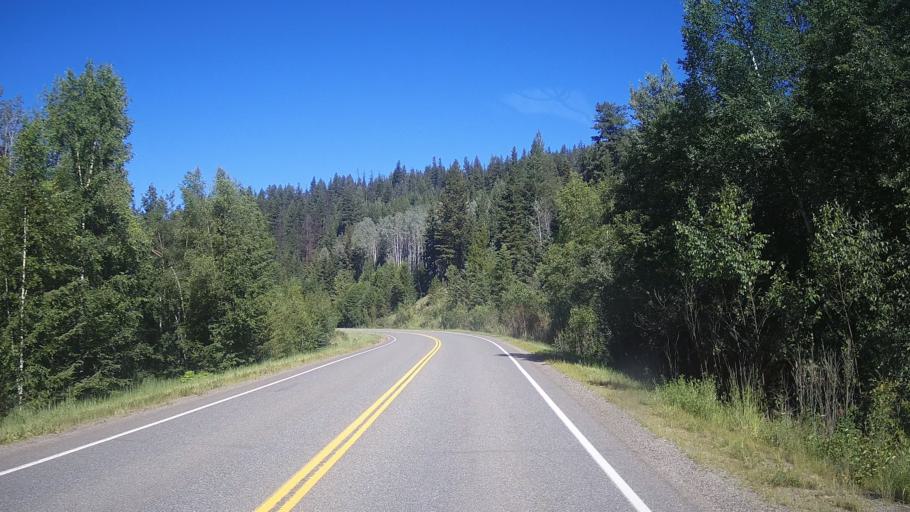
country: CA
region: British Columbia
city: Kamloops
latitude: 51.4725
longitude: -120.5397
